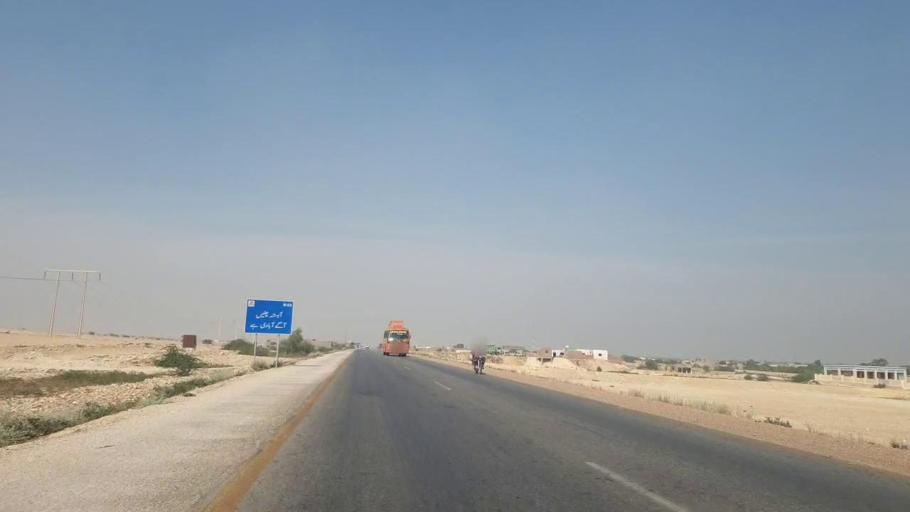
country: PK
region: Sindh
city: Hala
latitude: 25.7885
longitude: 68.2819
